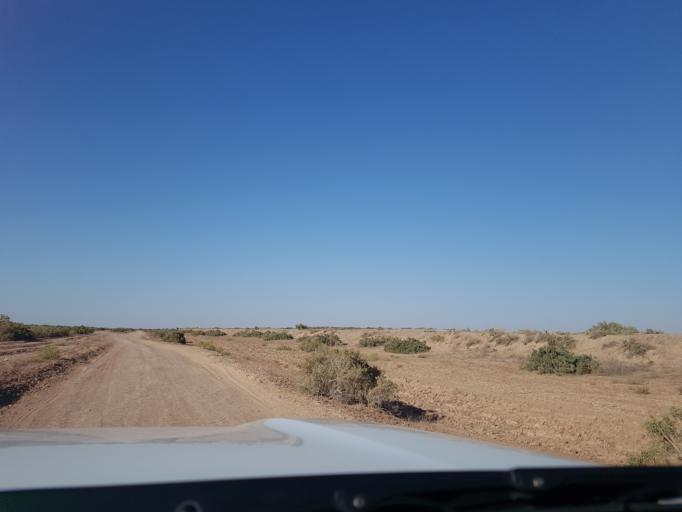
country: IR
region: Razavi Khorasan
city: Sarakhs
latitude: 36.9835
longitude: 61.3865
